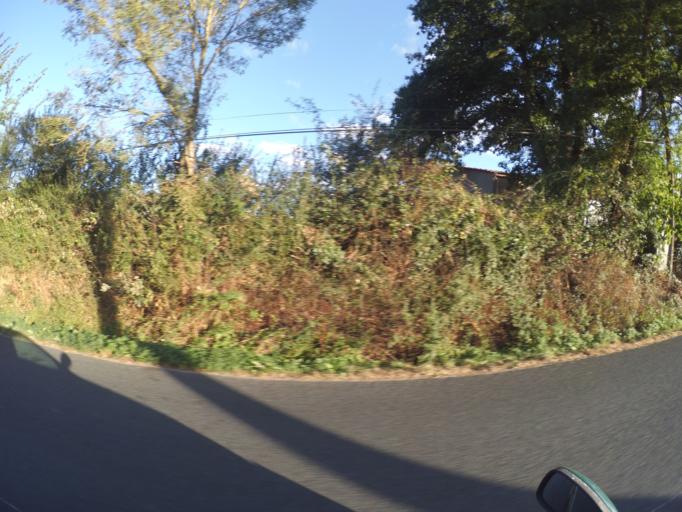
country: FR
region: Pays de la Loire
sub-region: Departement de la Vendee
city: Saint-Hilaire-de-Loulay
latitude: 46.9926
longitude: -1.3490
